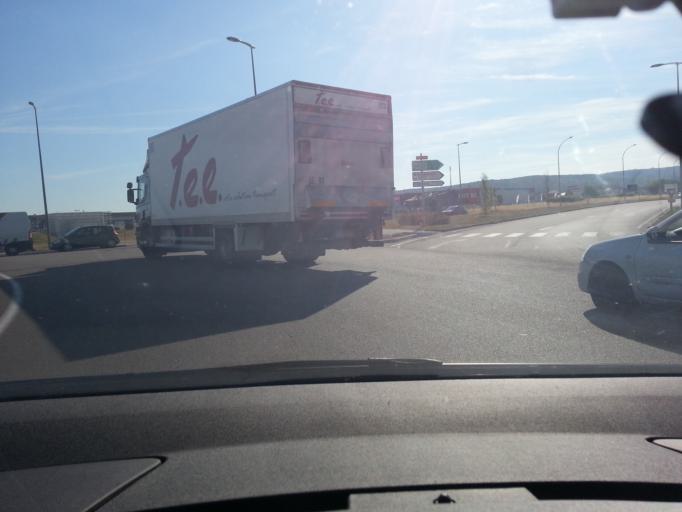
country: FR
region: Bourgogne
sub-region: Departement de la Cote-d'Or
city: Chenove
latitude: 47.2818
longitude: 5.0165
